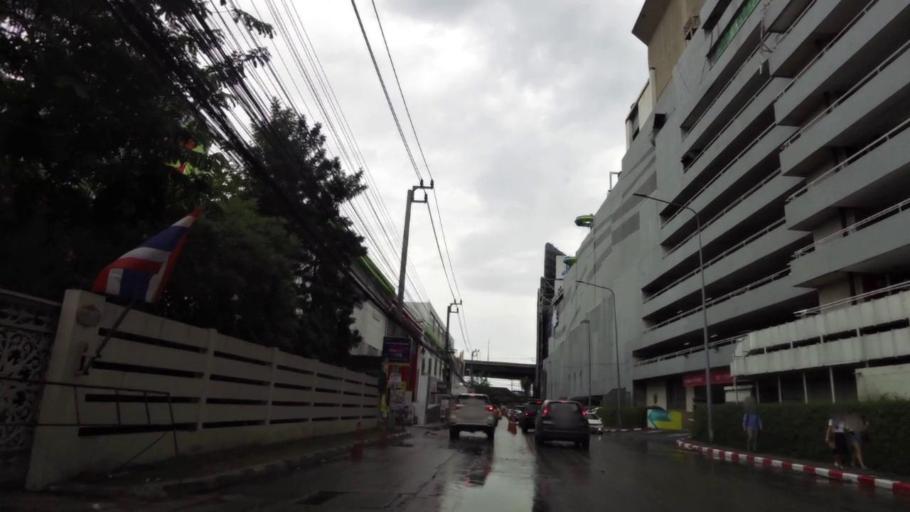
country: TH
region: Bangkok
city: Bang Na
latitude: 13.6698
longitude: 100.6354
